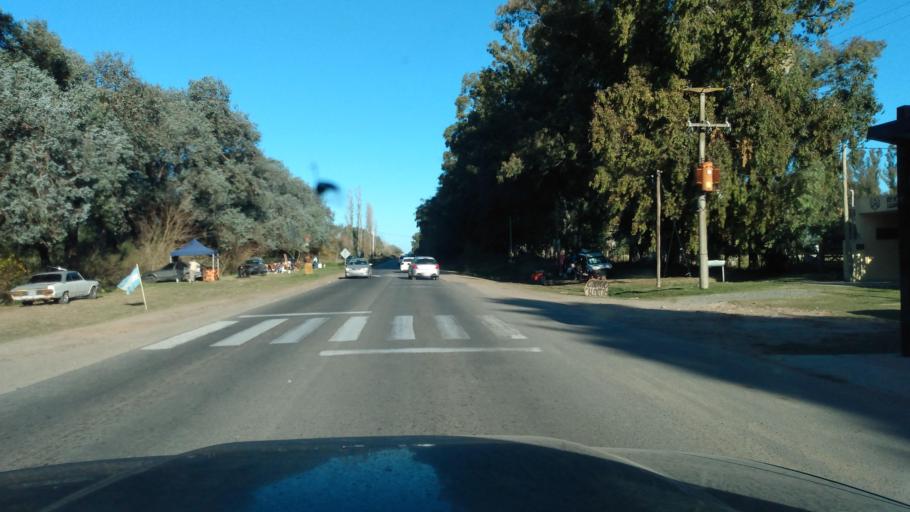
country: AR
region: Buenos Aires
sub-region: Partido de Lujan
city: Lujan
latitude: -34.5294
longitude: -59.1689
